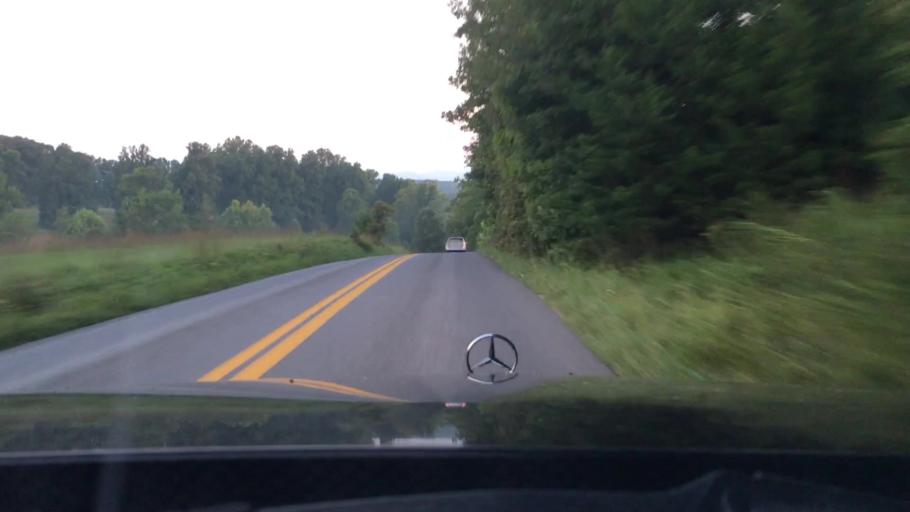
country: US
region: Virginia
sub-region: Campbell County
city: Timberlake
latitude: 37.2749
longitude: -79.2674
